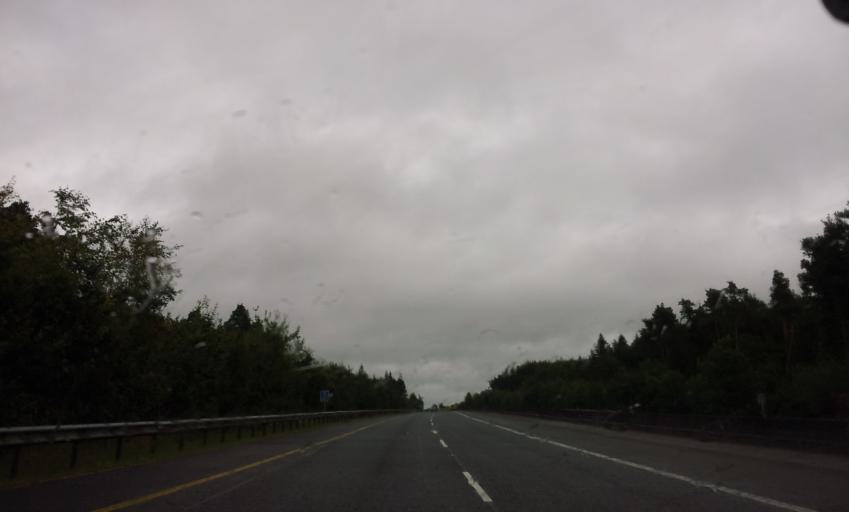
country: IE
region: Munster
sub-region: County Cork
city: Fermoy
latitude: 52.1206
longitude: -8.2693
